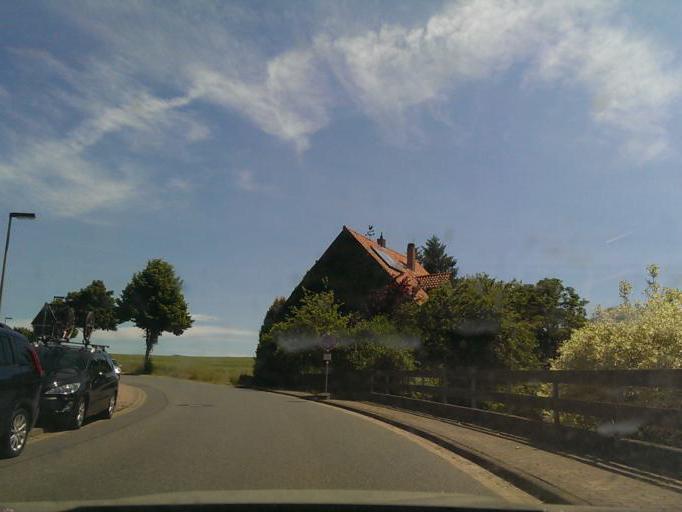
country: DE
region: Lower Saxony
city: Coppengrave
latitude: 51.9864
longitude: 9.7682
